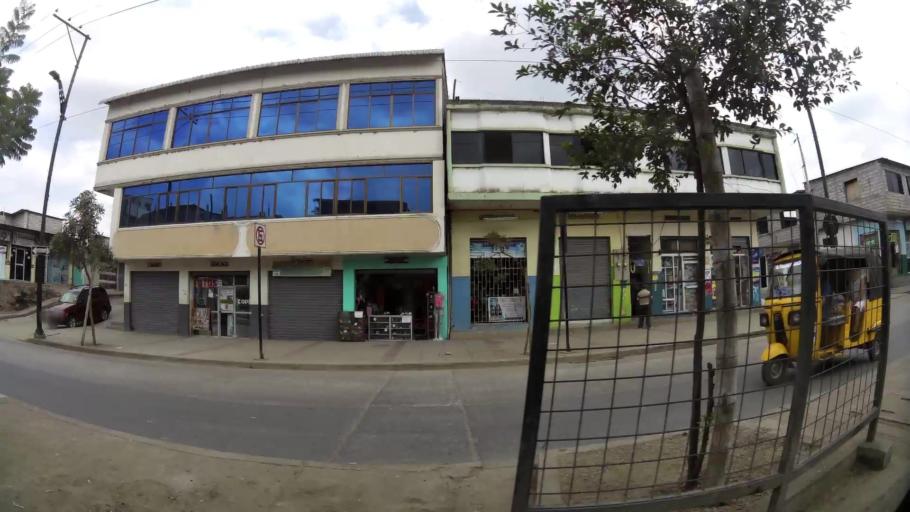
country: EC
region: Guayas
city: Santa Lucia
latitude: -2.1043
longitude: -79.9522
